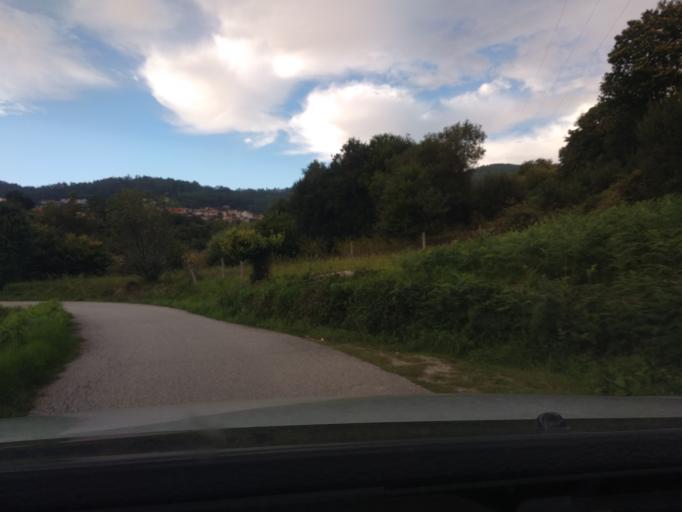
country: ES
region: Galicia
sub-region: Provincia de Pontevedra
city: Moana
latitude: 42.2981
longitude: -8.7349
